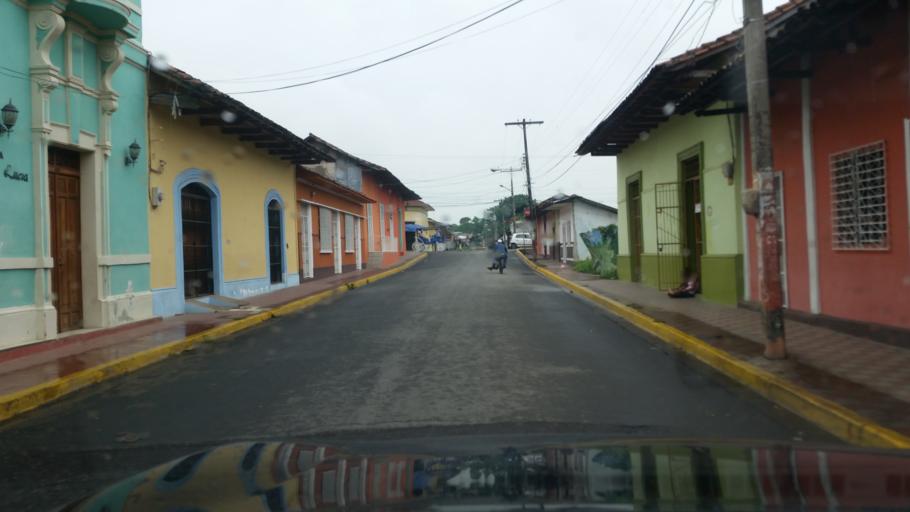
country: NI
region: Granada
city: Granada
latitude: 11.9337
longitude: -85.9546
